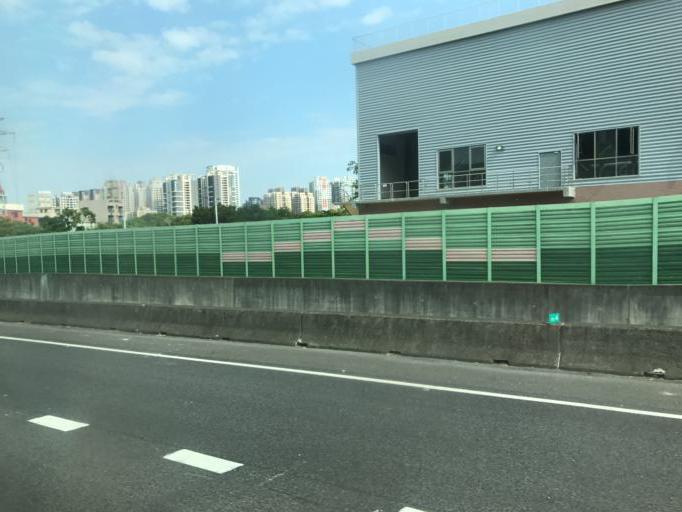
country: TW
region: Taiwan
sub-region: Hsinchu
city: Hsinchu
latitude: 24.7861
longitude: 121.0041
